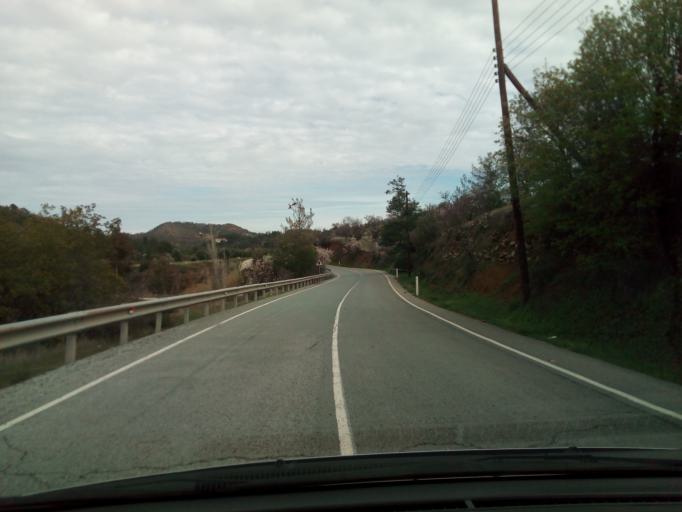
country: CY
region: Lefkosia
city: Klirou
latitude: 34.9789
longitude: 33.1543
